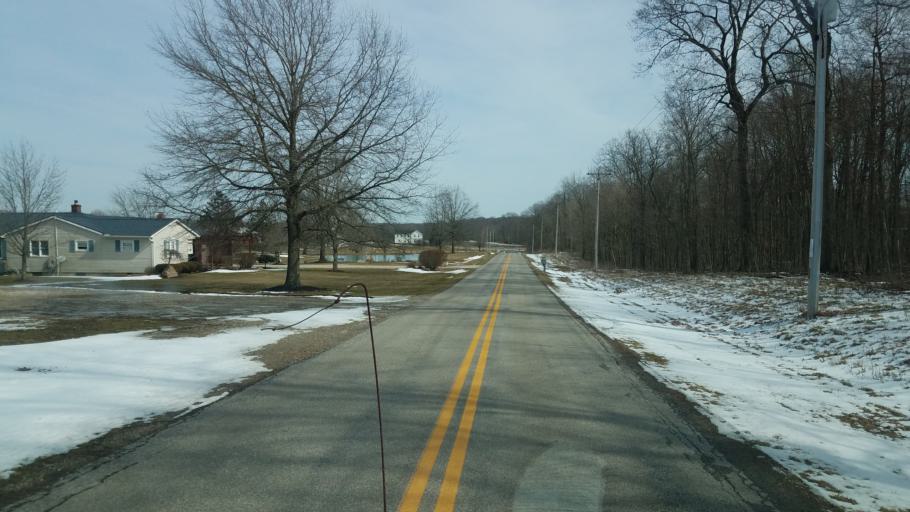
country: US
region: Ohio
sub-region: Delaware County
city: Ashley
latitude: 40.3515
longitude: -82.9468
